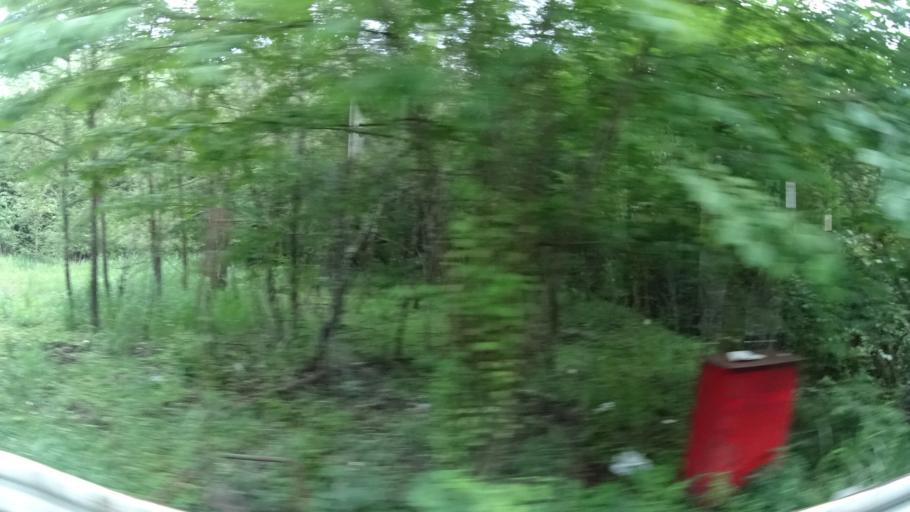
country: JP
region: Tochigi
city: Nikko
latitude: 36.6706
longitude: 139.4794
